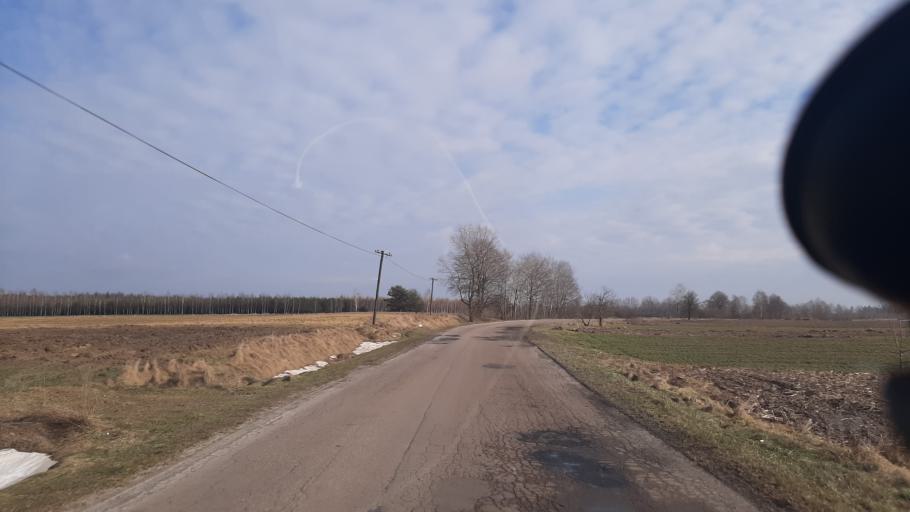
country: PL
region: Lublin Voivodeship
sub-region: Powiat lubartowski
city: Uscimow Stary
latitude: 51.4685
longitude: 22.9844
